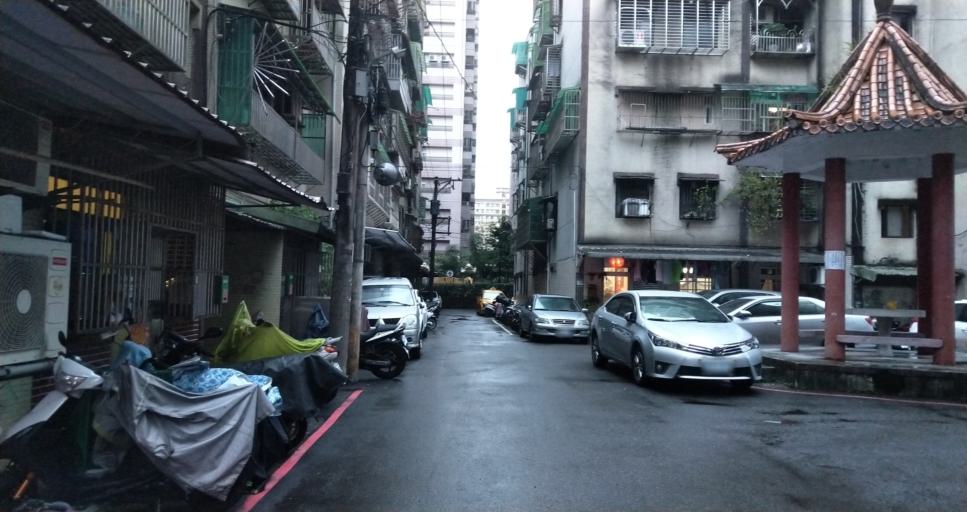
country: TW
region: Taiwan
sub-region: Keelung
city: Keelung
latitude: 25.0634
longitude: 121.6526
